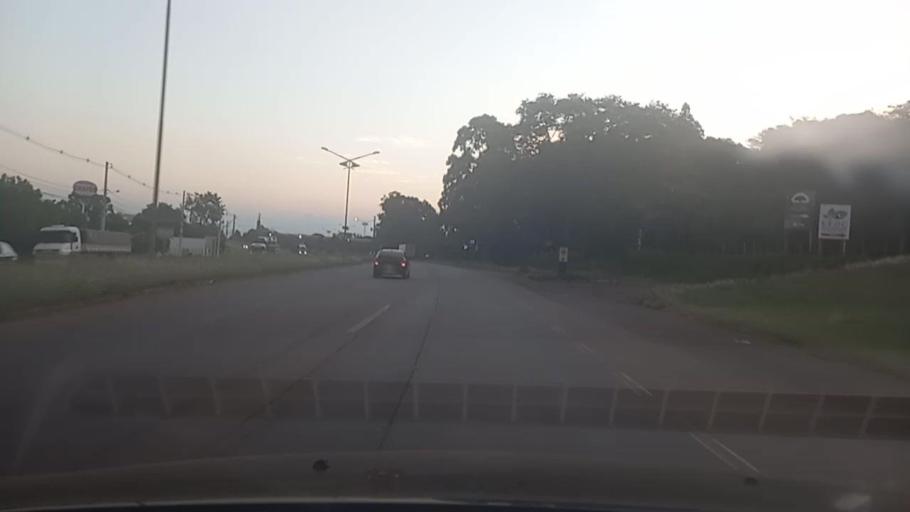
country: BR
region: Rio Grande do Sul
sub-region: Passo Fundo
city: Passo Fundo
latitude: -28.2751
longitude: -52.4482
